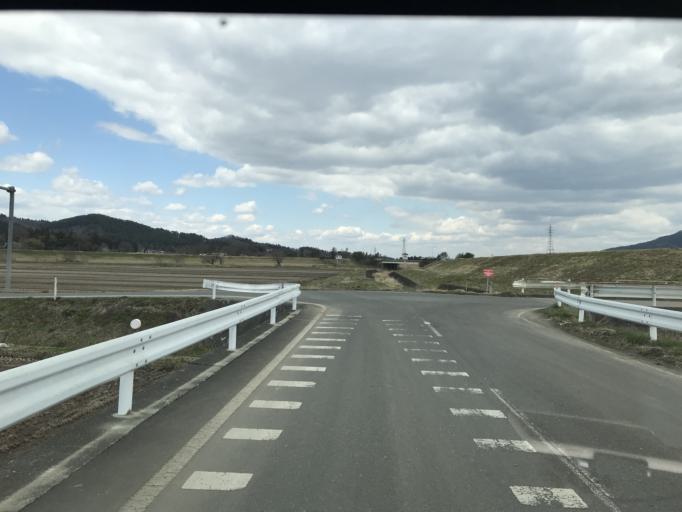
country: JP
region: Iwate
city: Ichinoseki
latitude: 38.9754
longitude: 141.1075
